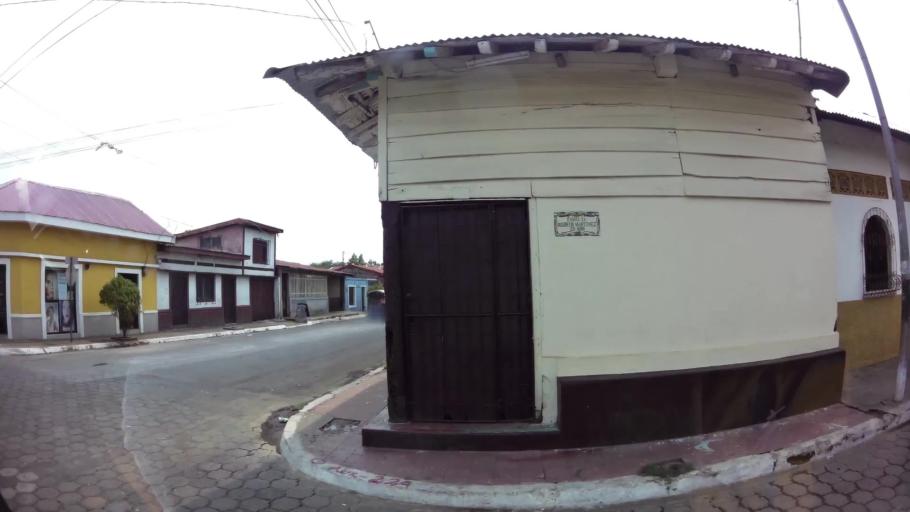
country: NI
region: Chinandega
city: Chinandega
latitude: 12.6289
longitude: -87.1353
